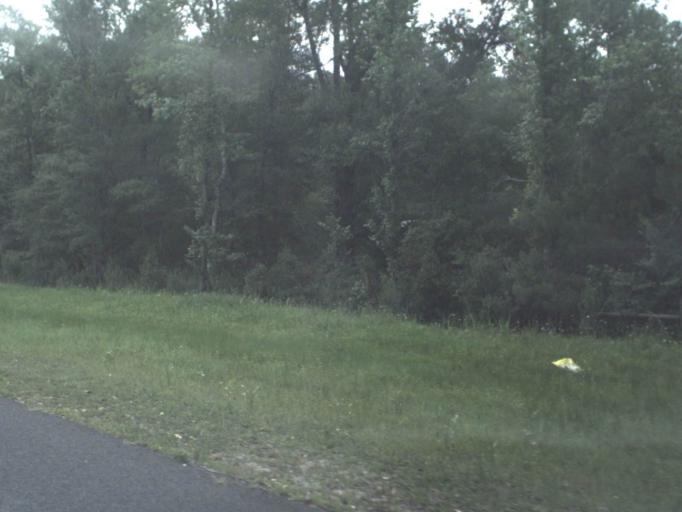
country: US
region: Florida
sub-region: Nassau County
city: Callahan
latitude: 30.6027
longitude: -81.7528
